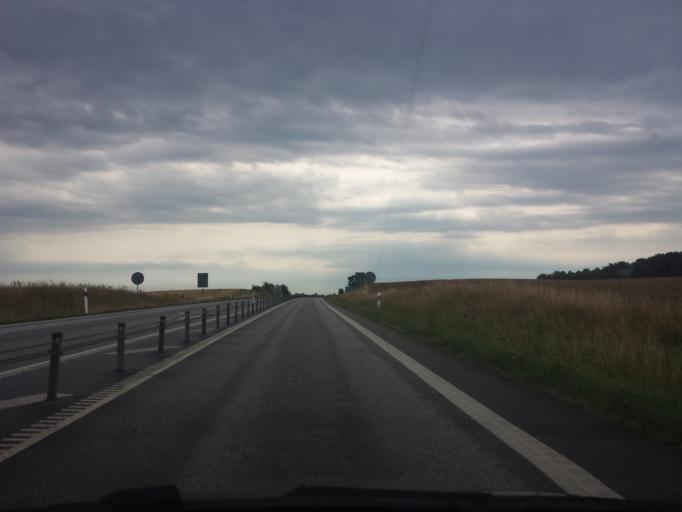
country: SE
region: Skane
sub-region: Ystads Kommun
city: Ystad
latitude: 55.4679
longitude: 13.7091
